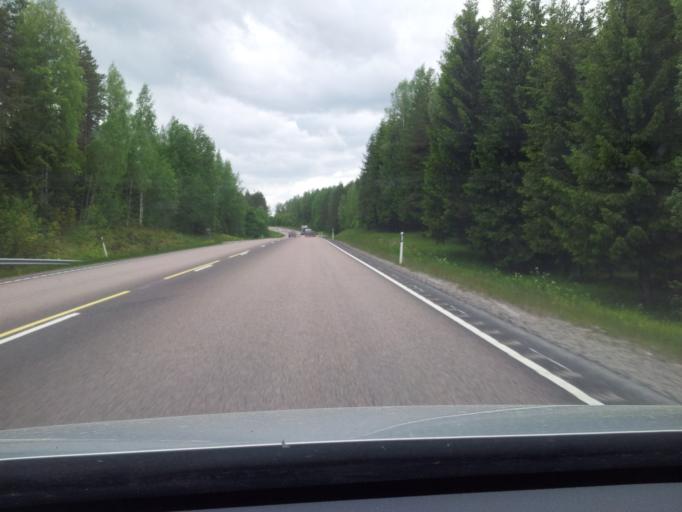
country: FI
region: South Karelia
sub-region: Lappeenranta
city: Taavetti
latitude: 60.9134
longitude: 27.3729
